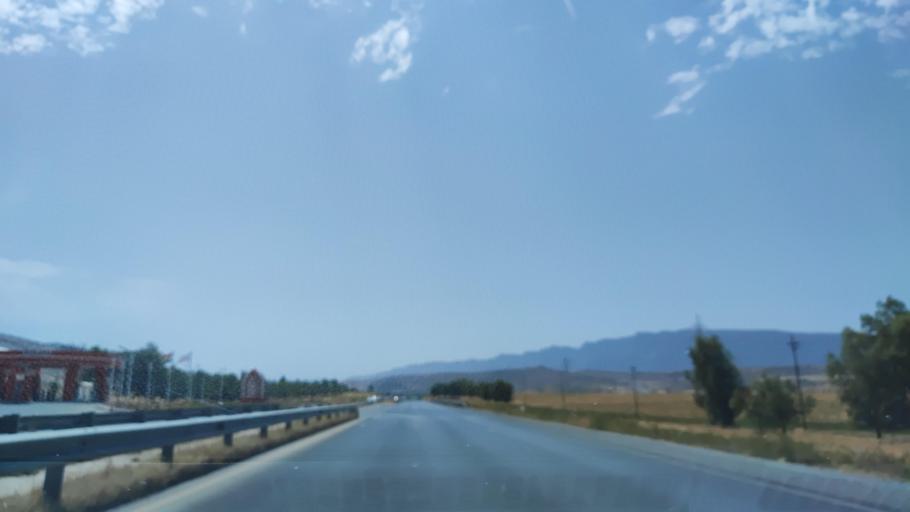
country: IQ
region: Arbil
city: Shaqlawah
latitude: 36.4711
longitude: 44.3816
